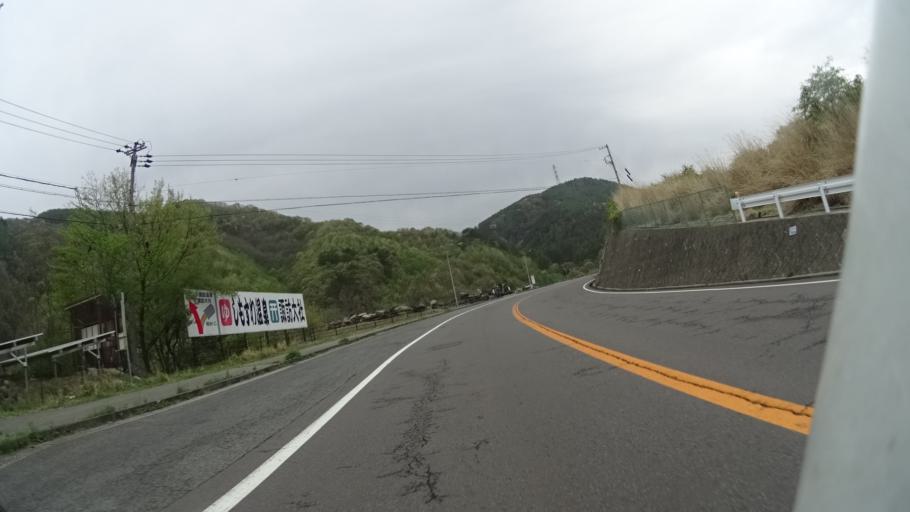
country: JP
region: Nagano
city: Suwa
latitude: 36.1189
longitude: 138.1018
